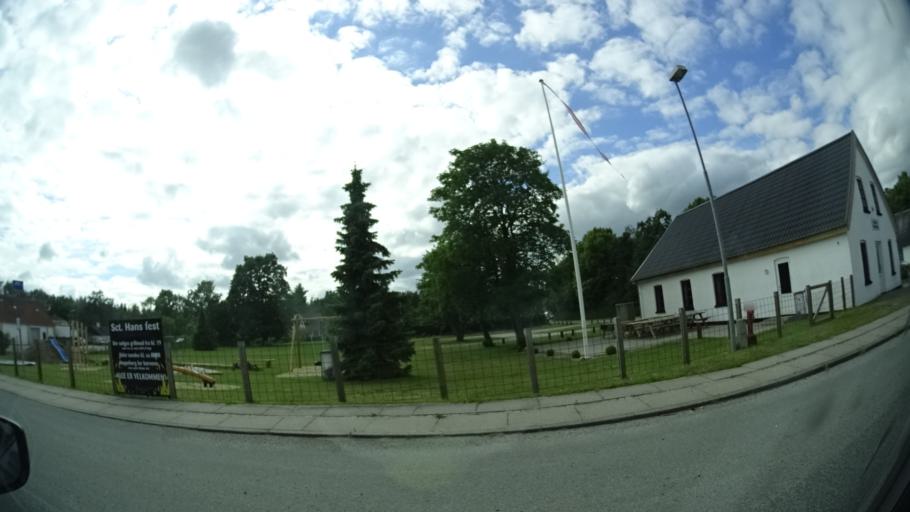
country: DK
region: Central Jutland
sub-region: Syddjurs Kommune
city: Ryomgard
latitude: 56.3688
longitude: 10.4986
